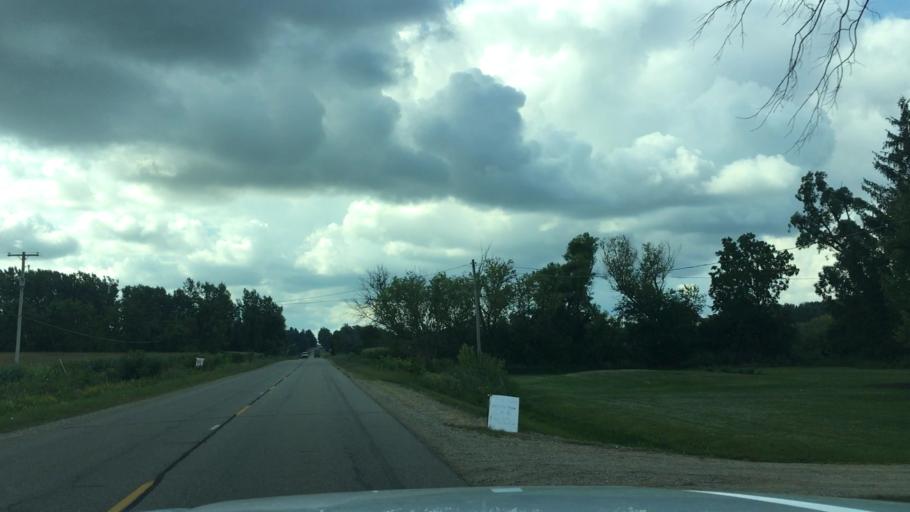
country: US
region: Michigan
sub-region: Ottawa County
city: Hudsonville
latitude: 42.7906
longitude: -85.8418
